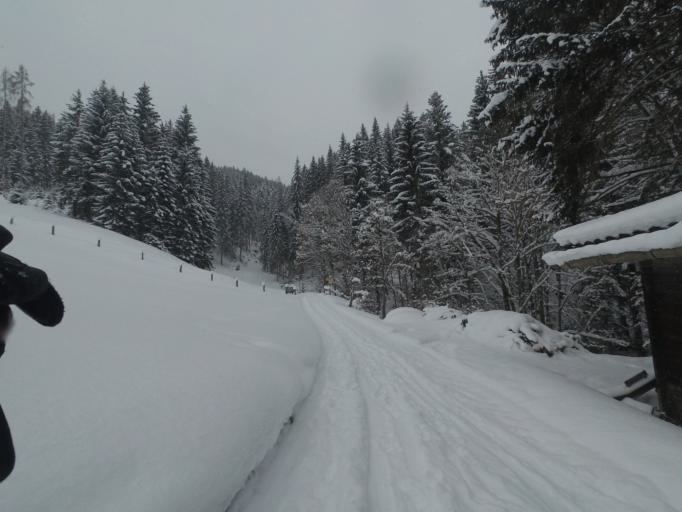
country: AT
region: Salzburg
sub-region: Politischer Bezirk Sankt Johann im Pongau
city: Wagrain
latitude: 47.3294
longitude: 13.2844
